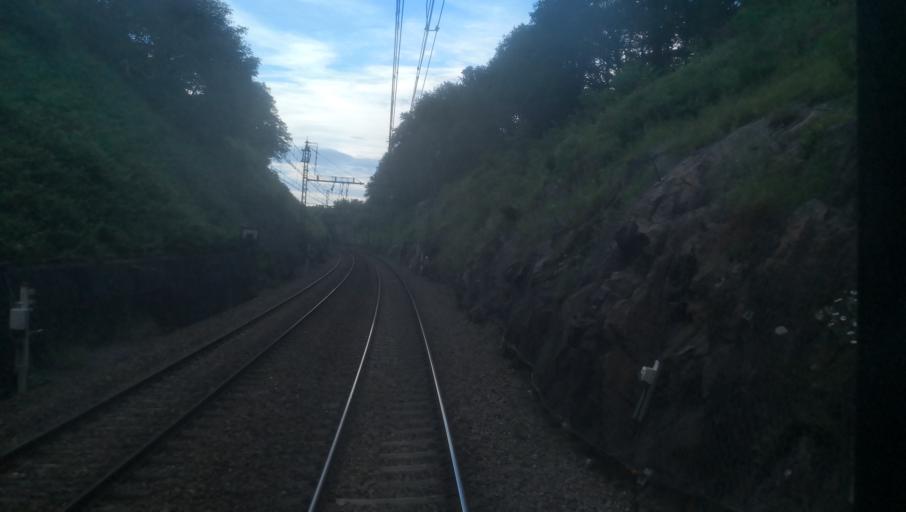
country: FR
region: Limousin
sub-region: Departement de la Creuse
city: La Souterraine
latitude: 46.2247
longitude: 1.4939
